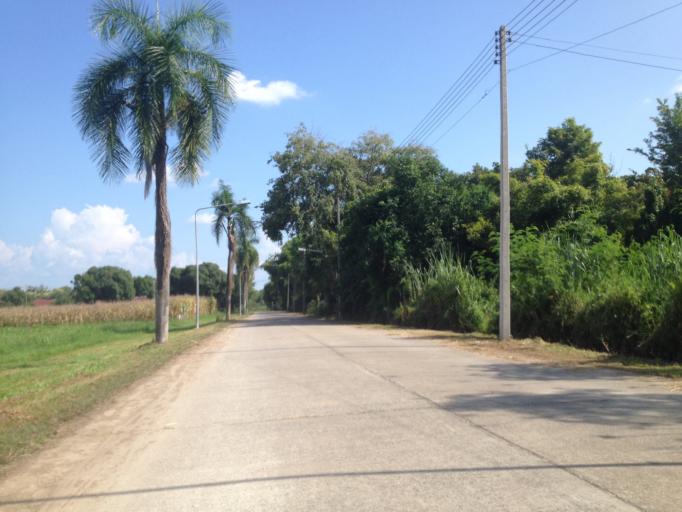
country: TH
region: Chiang Mai
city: Chiang Mai
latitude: 18.7590
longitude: 98.9269
